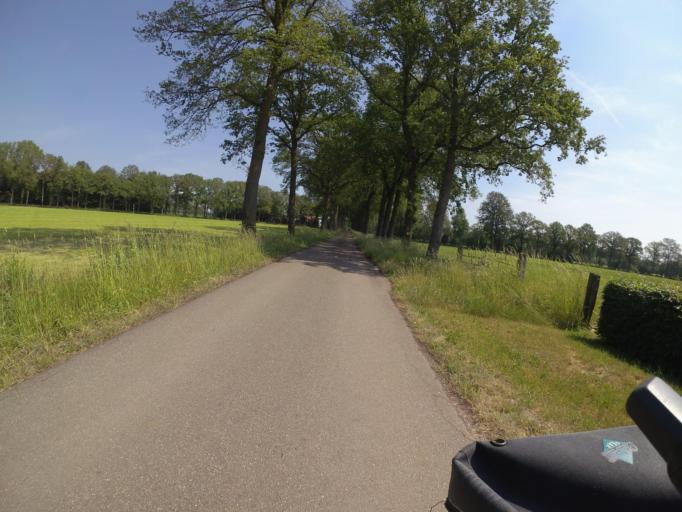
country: NL
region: Gelderland
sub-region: Berkelland
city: Neede
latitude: 52.1373
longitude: 6.6476
